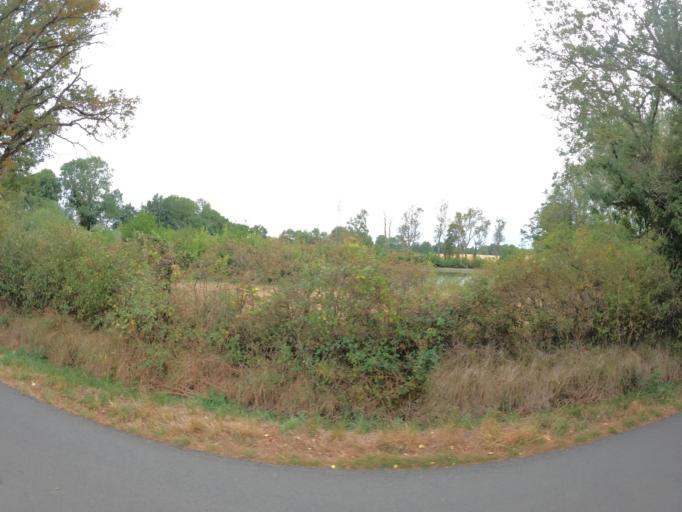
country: FR
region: Pays de la Loire
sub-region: Departement de Maine-et-Loire
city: Saint-Christophe-du-Bois
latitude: 47.0425
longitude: -0.9777
